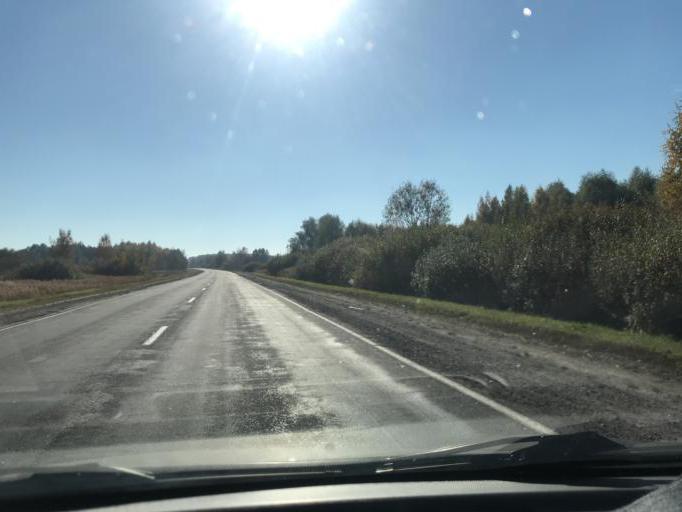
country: BY
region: Gomel
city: Kastsyukowka
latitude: 52.4464
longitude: 30.8249
